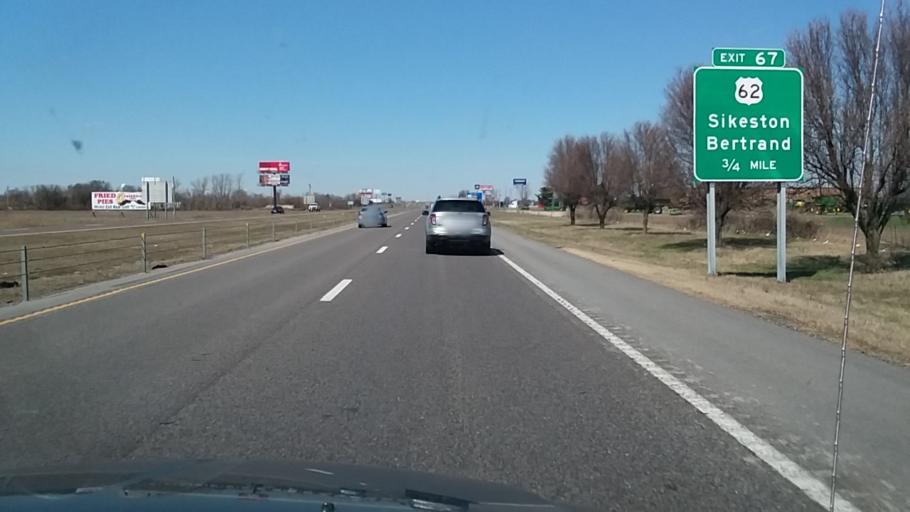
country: US
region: Missouri
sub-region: Scott County
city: Sikeston
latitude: 36.8810
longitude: -89.5330
